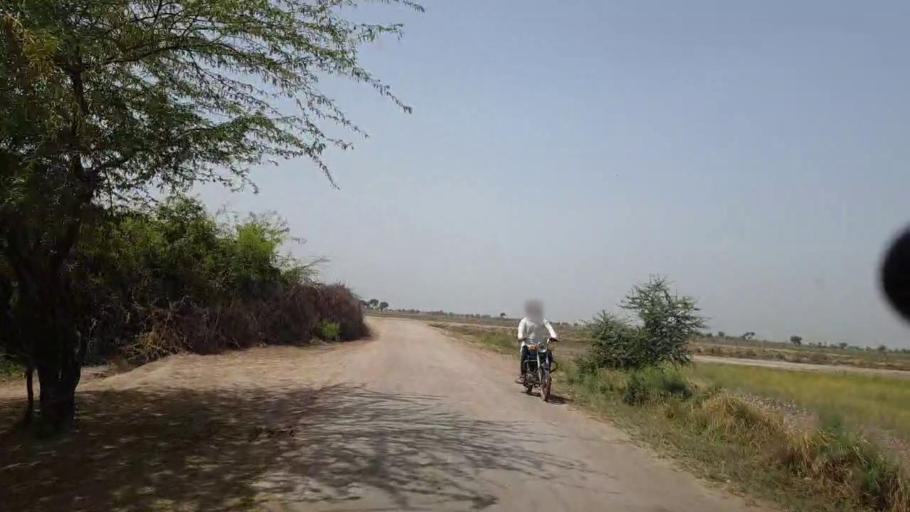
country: PK
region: Sindh
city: Matli
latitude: 25.0633
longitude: 68.6921
